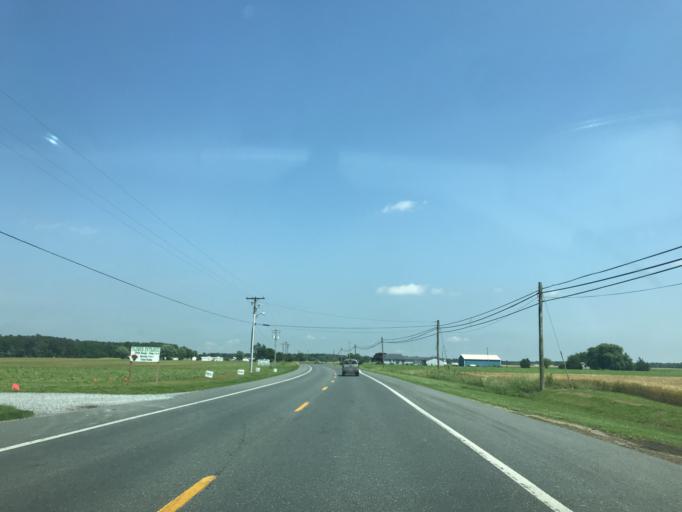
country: US
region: Maryland
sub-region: Dorchester County
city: Hurlock
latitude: 38.5835
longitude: -75.8558
